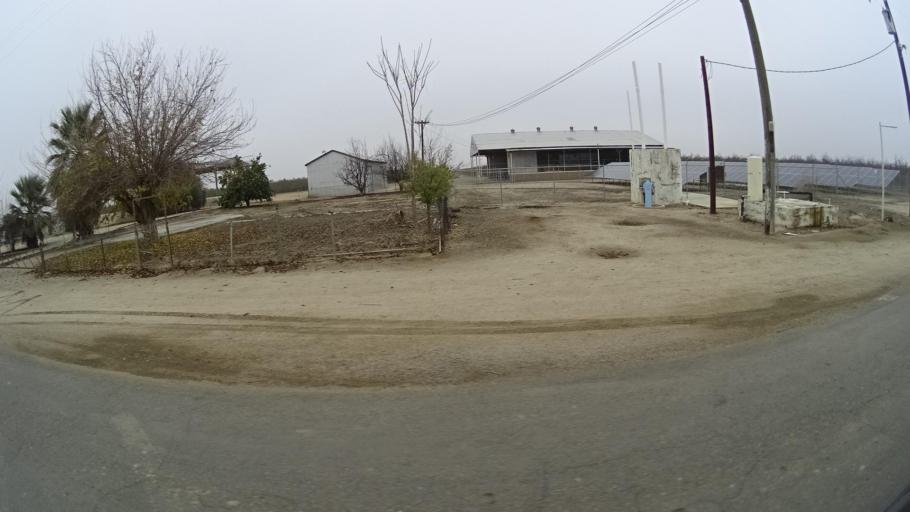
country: US
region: California
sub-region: Kern County
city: Wasco
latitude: 35.5756
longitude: -119.5095
